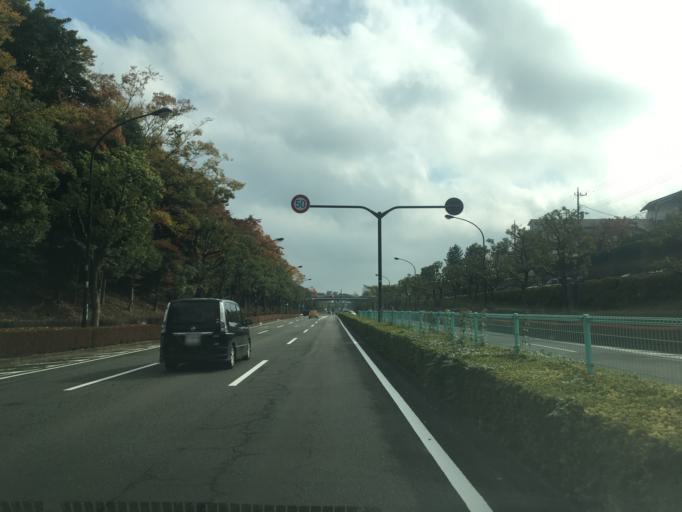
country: JP
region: Tokyo
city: Hino
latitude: 35.6137
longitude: 139.4226
